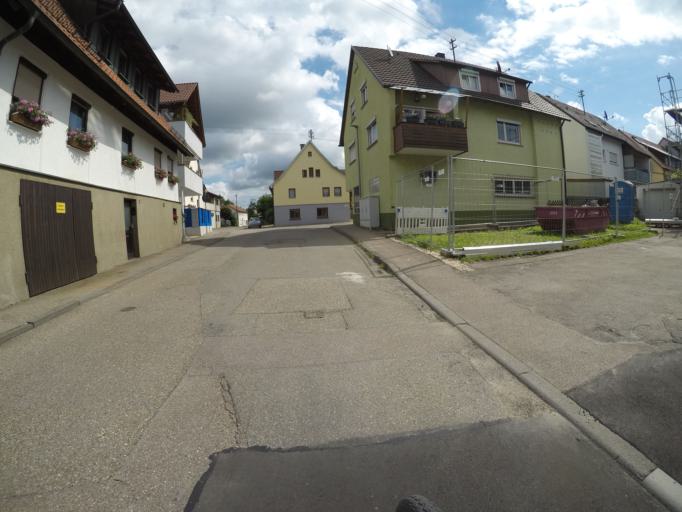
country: DE
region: Baden-Wuerttemberg
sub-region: Regierungsbezirk Stuttgart
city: Denkendorf
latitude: 48.7197
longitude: 9.3236
